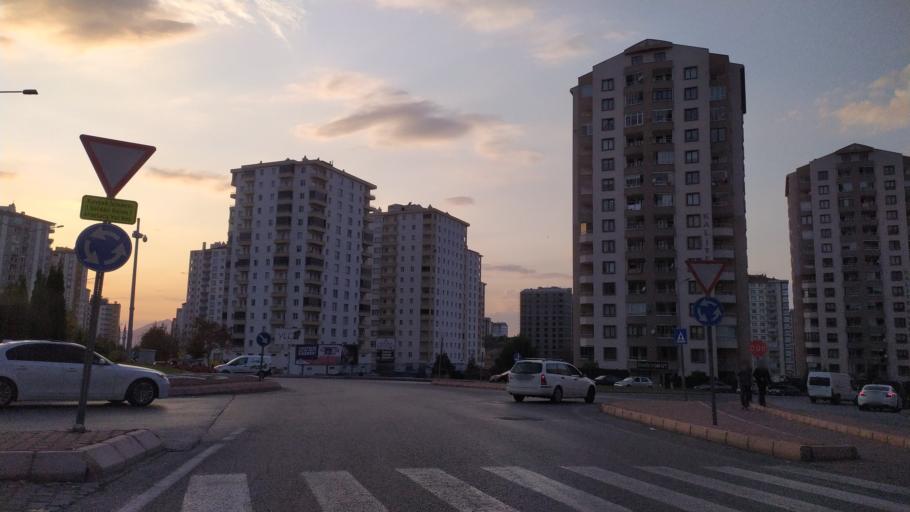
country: TR
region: Kayseri
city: Talas
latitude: 38.7086
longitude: 35.5612
